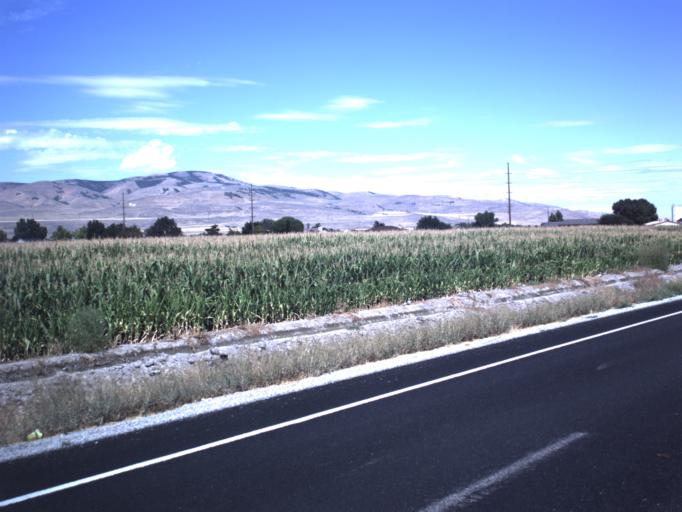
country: US
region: Utah
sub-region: Box Elder County
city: Garland
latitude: 41.7245
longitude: -112.1428
